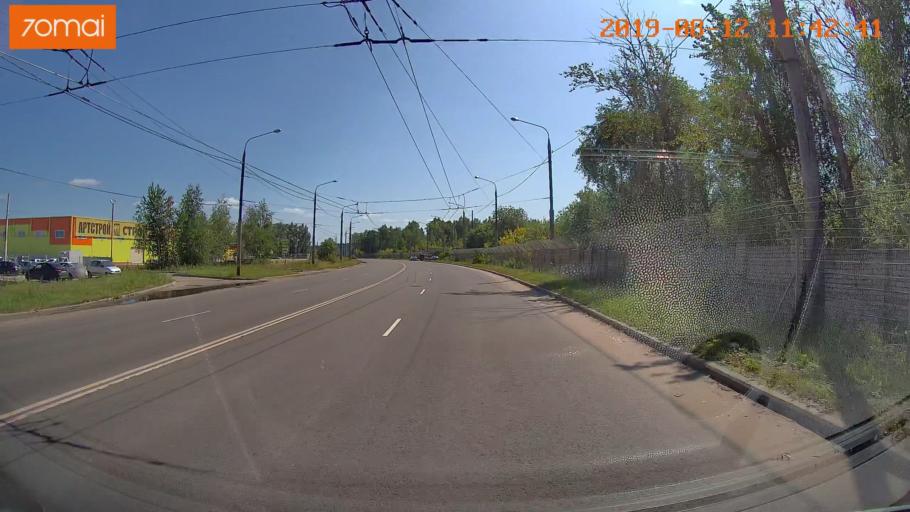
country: RU
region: Ivanovo
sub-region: Gorod Ivanovo
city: Ivanovo
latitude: 56.9475
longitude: 40.9655
